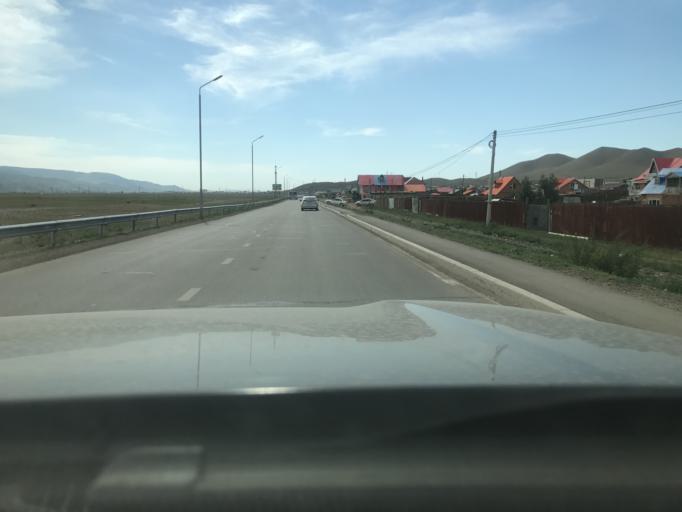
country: MN
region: Ulaanbaatar
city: Ulaanbaatar
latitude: 47.9158
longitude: 107.0816
